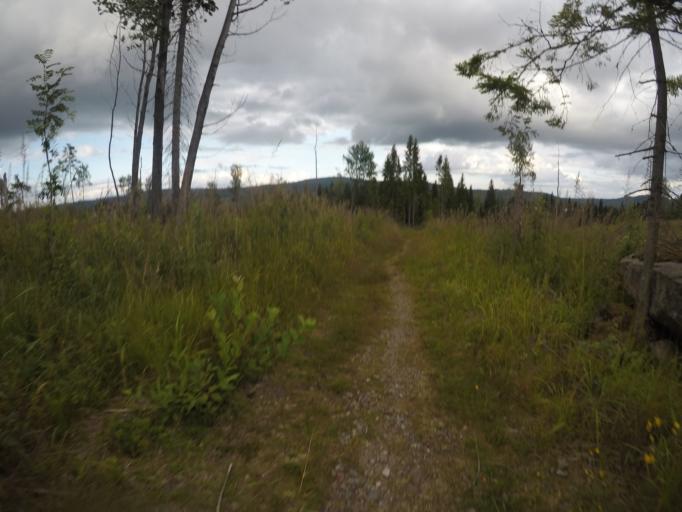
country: SE
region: Vaermland
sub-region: Filipstads Kommun
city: Lesjofors
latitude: 60.1541
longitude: 14.3904
